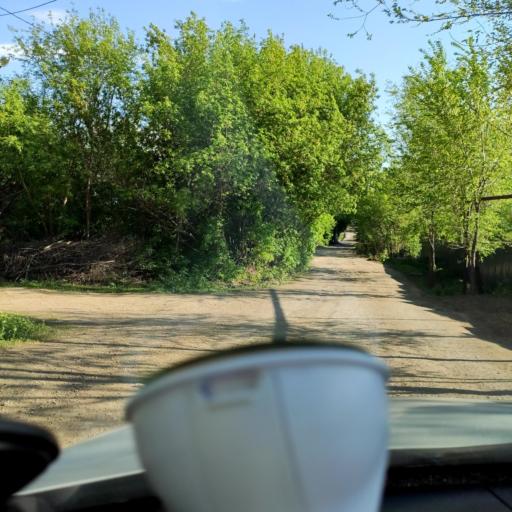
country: RU
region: Samara
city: Petra-Dubrava
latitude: 53.2572
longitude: 50.3440
